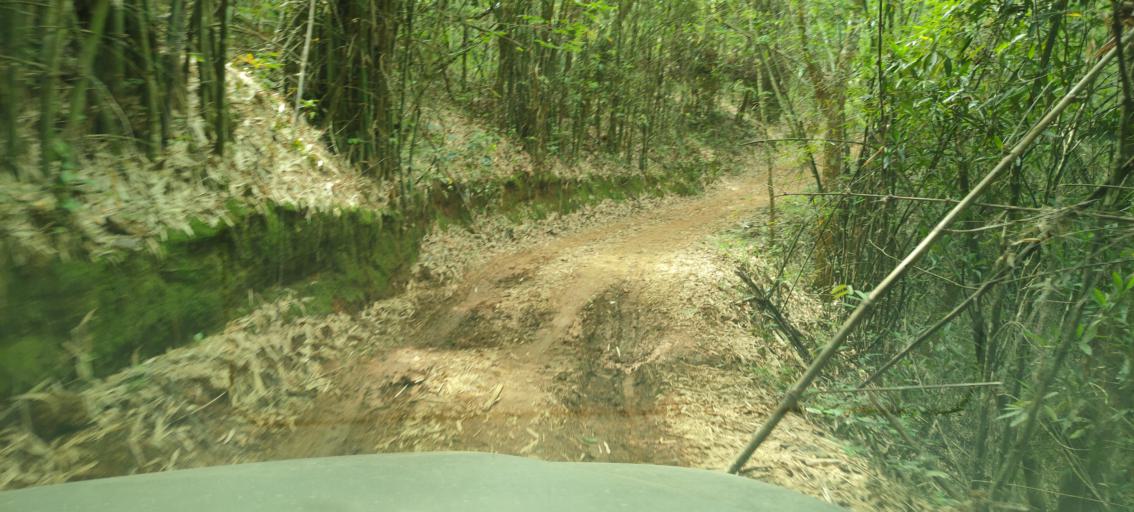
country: LA
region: Loungnamtha
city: Muang Nale
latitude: 20.4156
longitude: 101.4734
